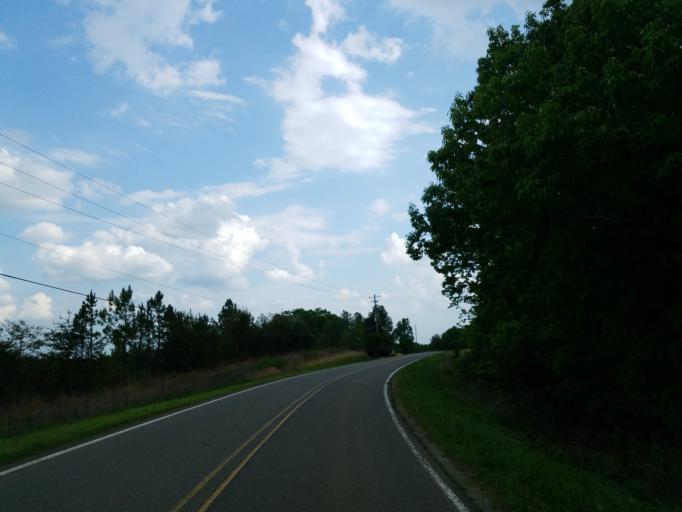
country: US
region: Georgia
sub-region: Pickens County
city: Jasper
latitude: 34.4442
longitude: -84.4524
